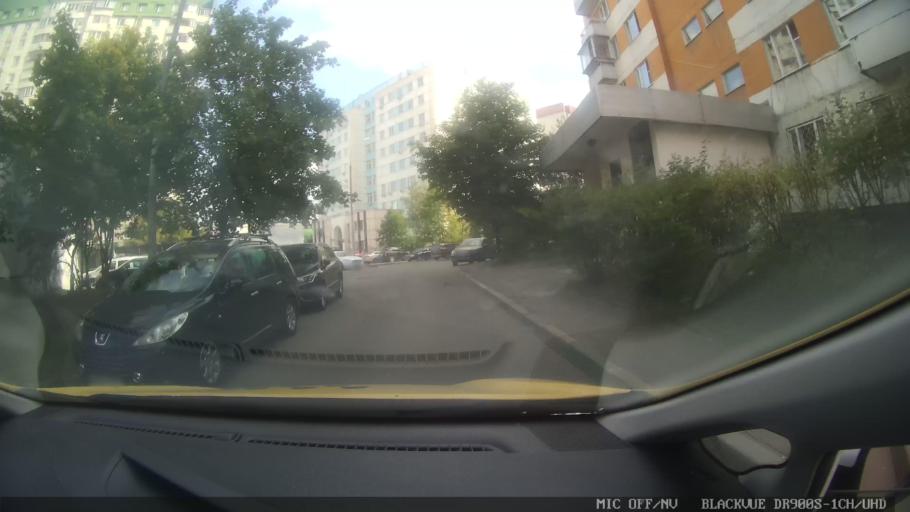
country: RU
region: Moscow
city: Zhulebino
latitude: 55.6838
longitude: 37.8489
